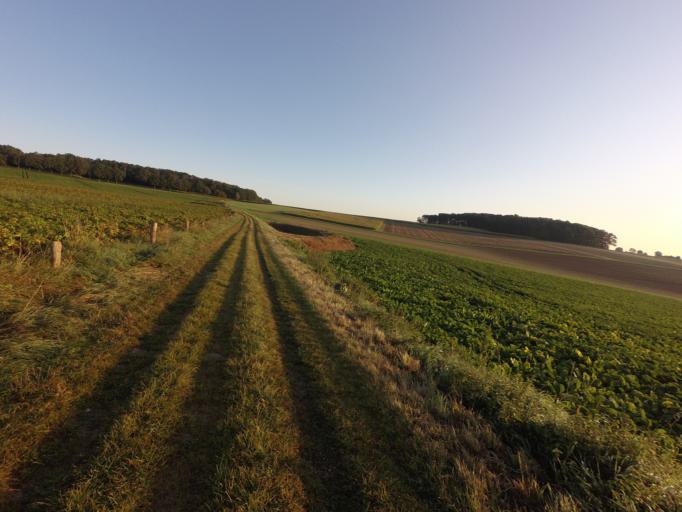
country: NL
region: Limburg
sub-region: Gemeente Voerendaal
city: Ubachsberg
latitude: 50.8424
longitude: 5.9561
